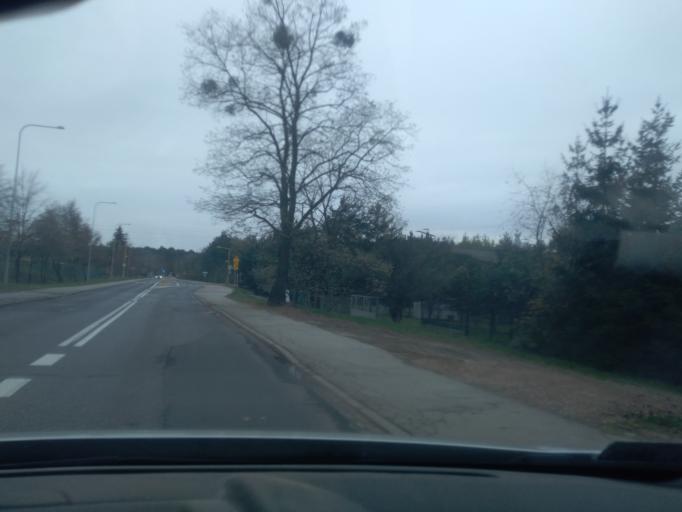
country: PL
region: Greater Poland Voivodeship
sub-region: Powiat poznanski
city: Murowana Goslina
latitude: 52.5444
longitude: 16.9727
